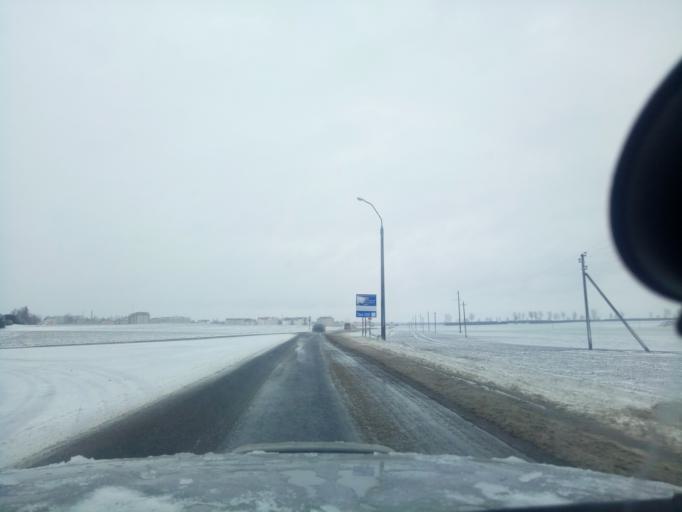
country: BY
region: Minsk
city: Nyasvizh
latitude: 53.2380
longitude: 26.6337
